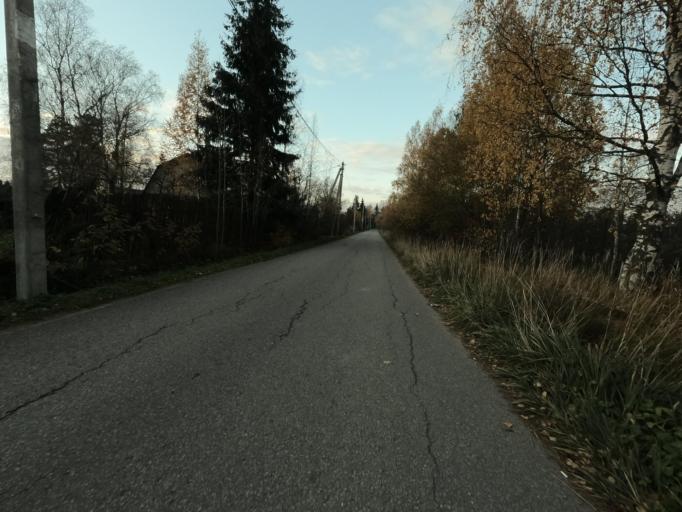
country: RU
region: Leningrad
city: Mga
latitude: 59.7784
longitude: 31.2050
